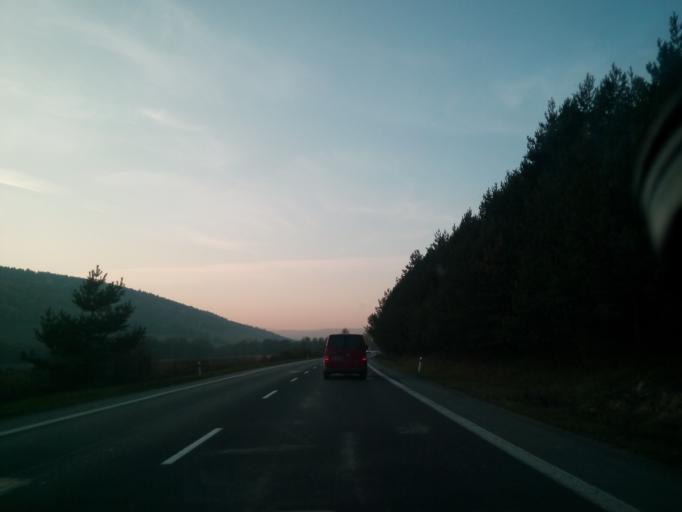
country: SK
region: Presovsky
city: Sabinov
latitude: 49.0119
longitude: 21.0519
